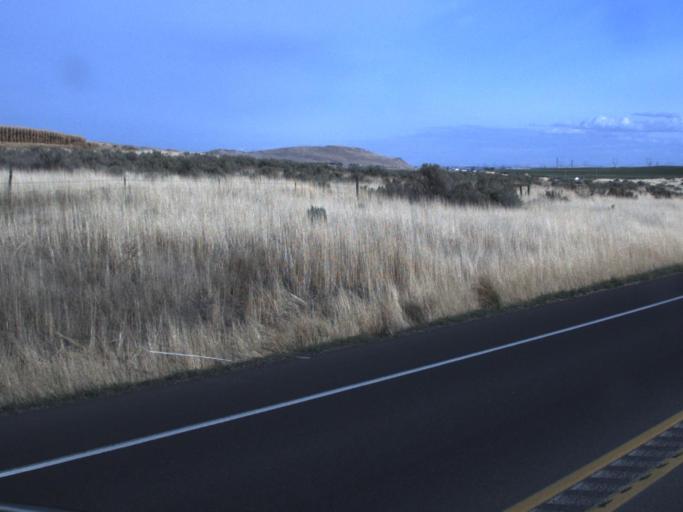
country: US
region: Oregon
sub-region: Umatilla County
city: Umatilla
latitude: 45.9498
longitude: -119.4013
